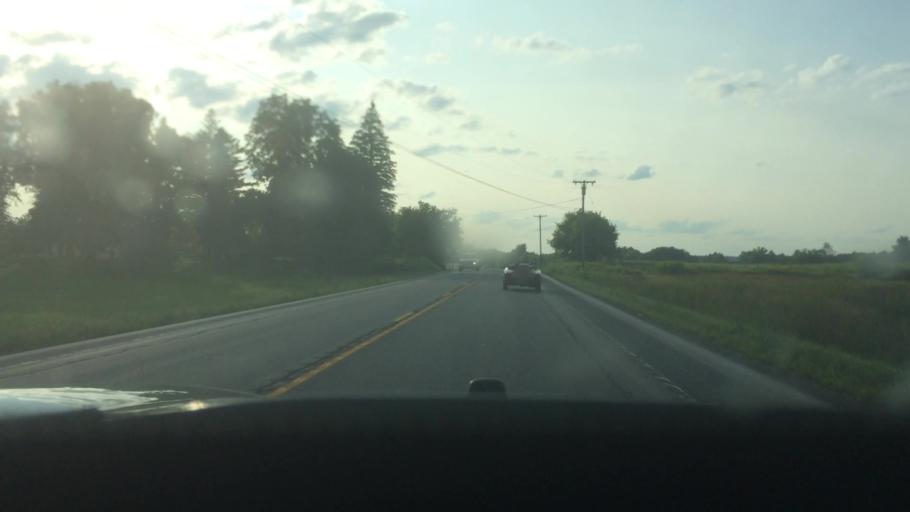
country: US
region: New York
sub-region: St. Lawrence County
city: Ogdensburg
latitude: 44.6588
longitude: -75.3282
